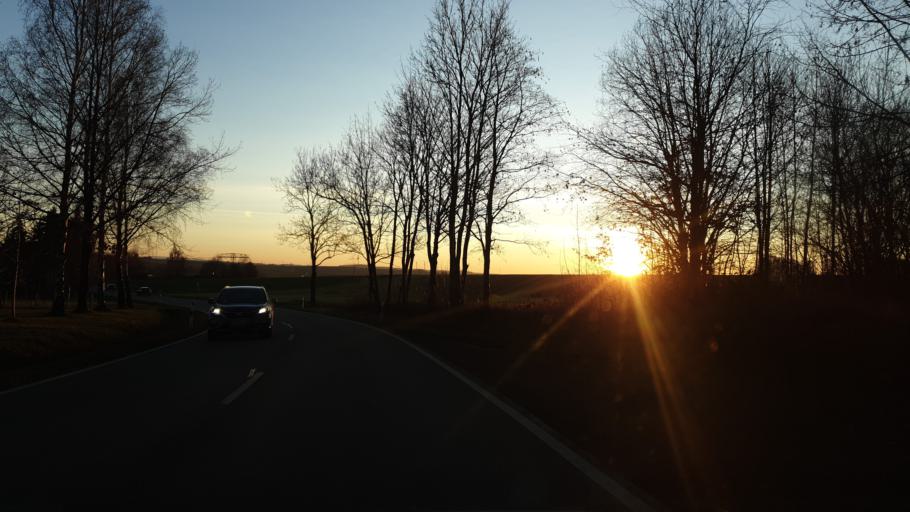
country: DE
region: Saxony
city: Kirchberg
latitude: 50.8013
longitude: 12.7573
